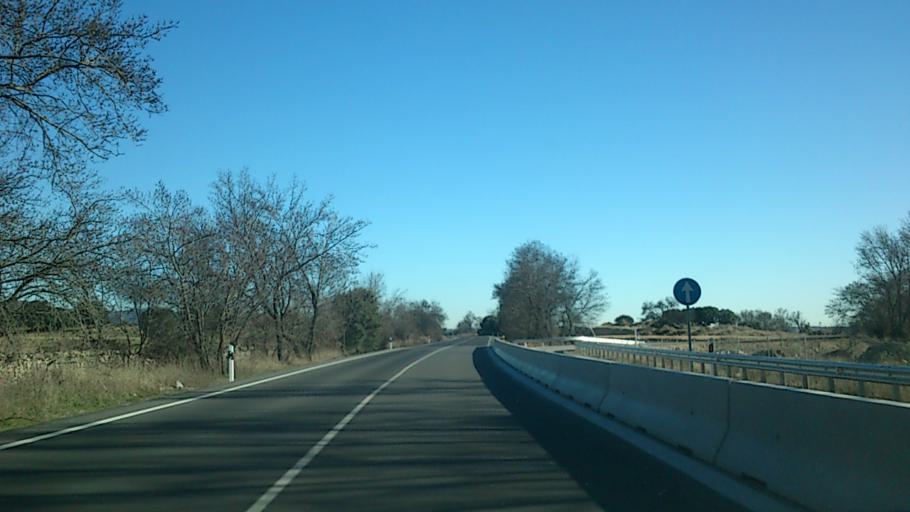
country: ES
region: Madrid
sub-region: Provincia de Madrid
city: Alpedrete
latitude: 40.6515
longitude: -4.0558
